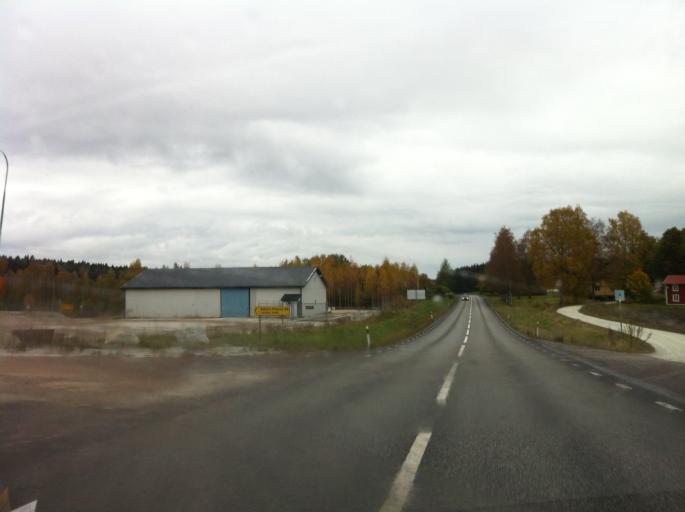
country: SE
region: OErebro
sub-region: Lindesbergs Kommun
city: Stora
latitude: 59.6688
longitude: 15.1006
